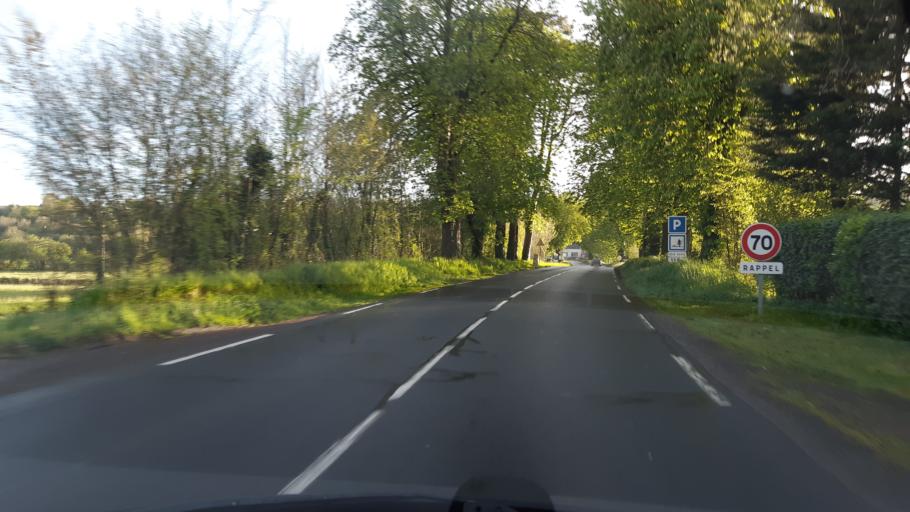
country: FR
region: Lower Normandy
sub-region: Departement de la Manche
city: Agneaux
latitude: 49.0900
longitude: -1.1193
